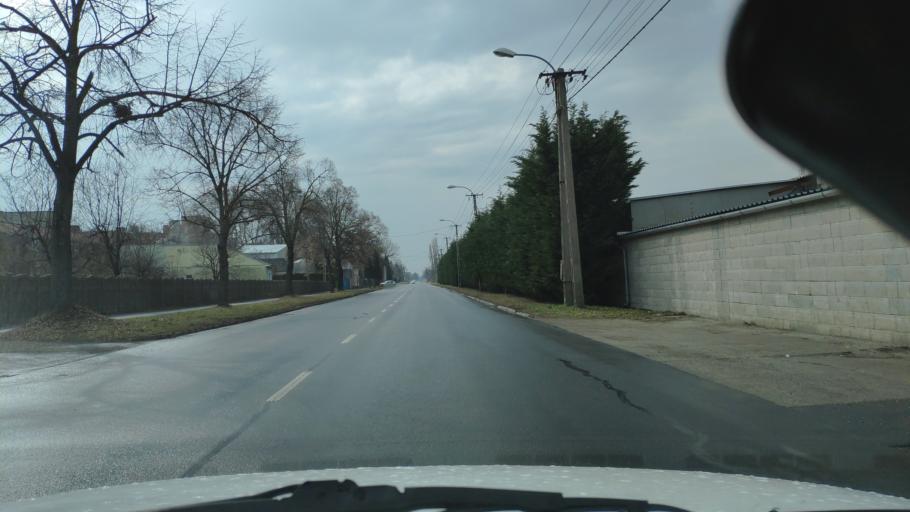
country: HU
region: Zala
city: Nagykanizsa
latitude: 46.4393
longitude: 16.9888
